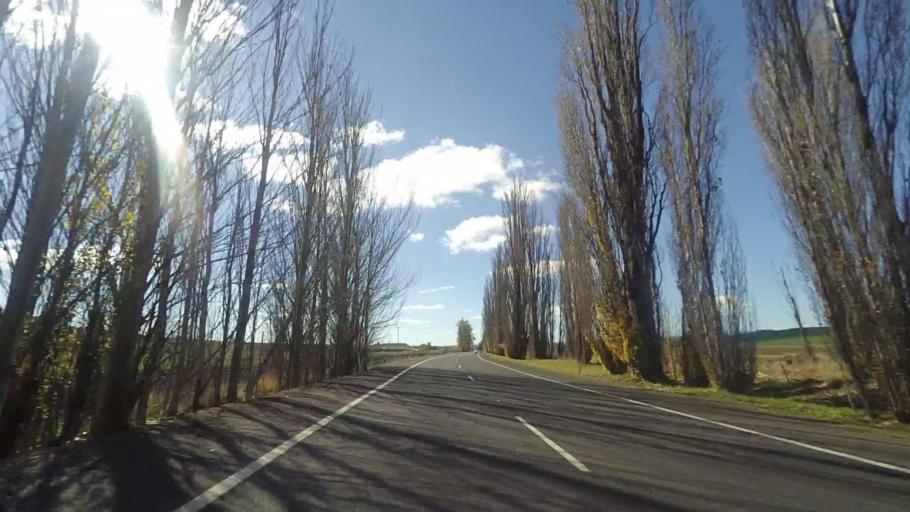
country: AU
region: New South Wales
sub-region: Bathurst Regional
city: Perthville
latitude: -33.4602
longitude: 149.5728
